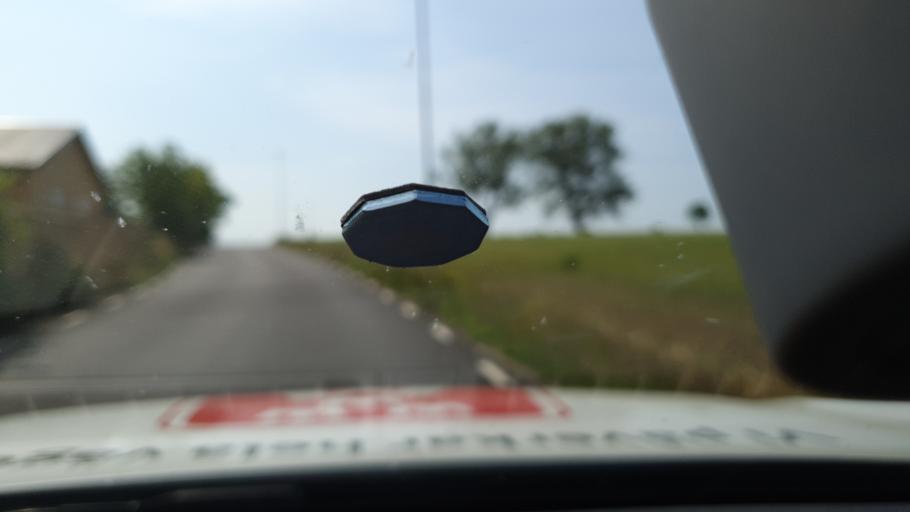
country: SE
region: Skane
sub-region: Burlovs Kommun
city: Arloev
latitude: 55.5979
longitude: 13.1331
